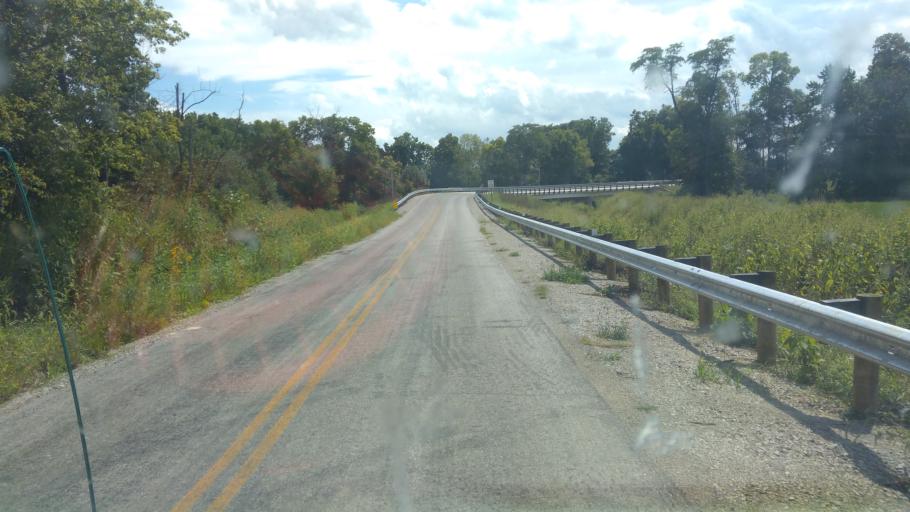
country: US
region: Ohio
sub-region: Union County
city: Richwood
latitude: 40.5953
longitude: -83.4094
